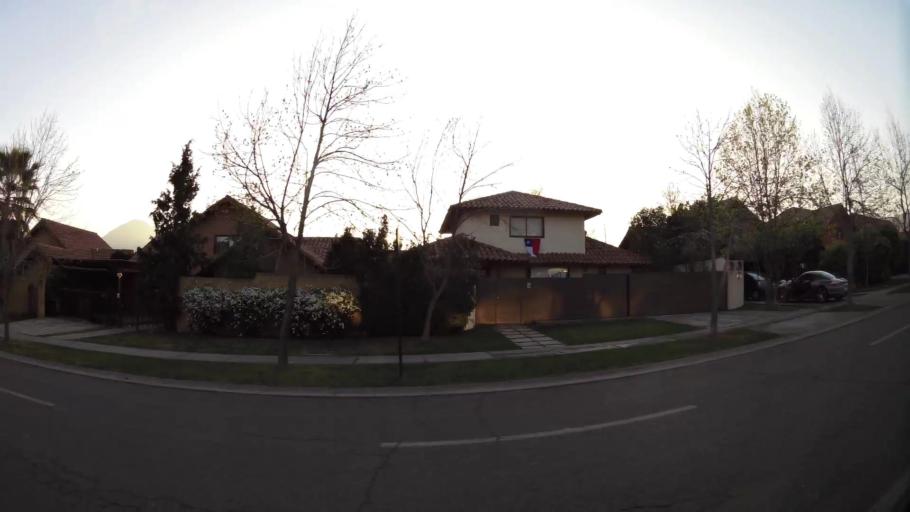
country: CL
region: Santiago Metropolitan
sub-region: Provincia de Chacabuco
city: Chicureo Abajo
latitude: -33.3250
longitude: -70.5387
